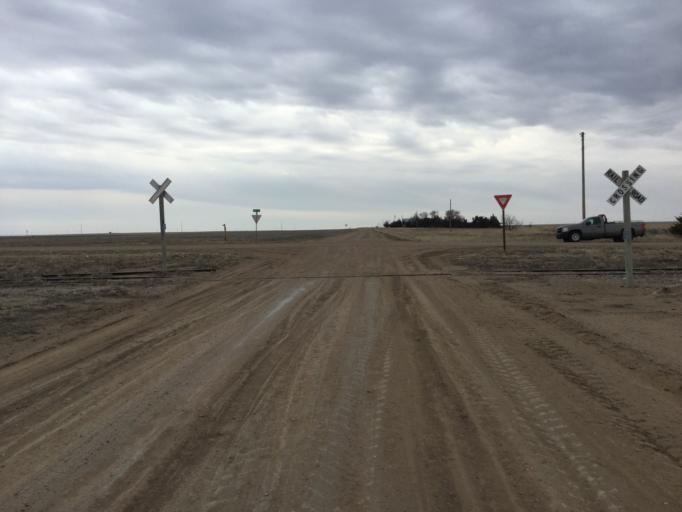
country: US
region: Kansas
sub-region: Stanton County
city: Johnson
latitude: 37.5629
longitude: -101.7080
